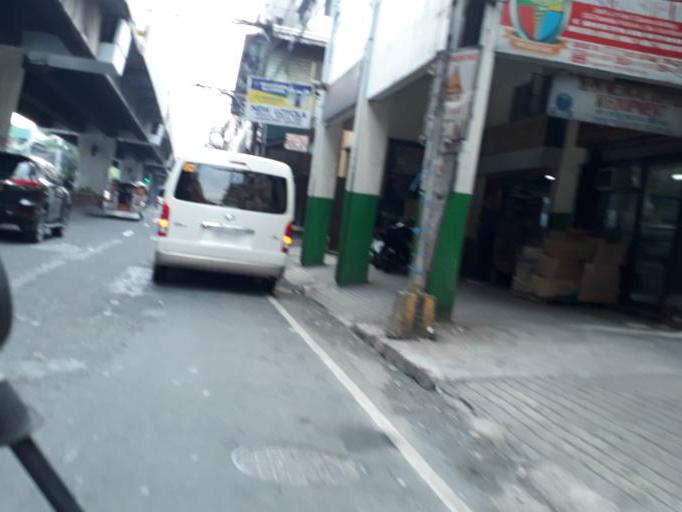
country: PH
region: Metro Manila
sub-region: City of Manila
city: Manila
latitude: 14.6122
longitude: 120.9826
